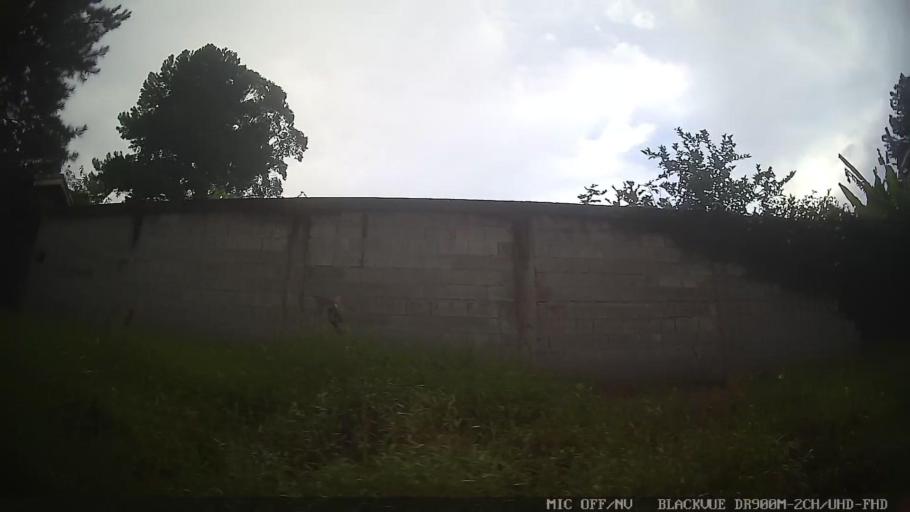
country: BR
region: Sao Paulo
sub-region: Rio Grande Da Serra
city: Rio Grande da Serra
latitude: -23.6888
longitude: -46.3128
